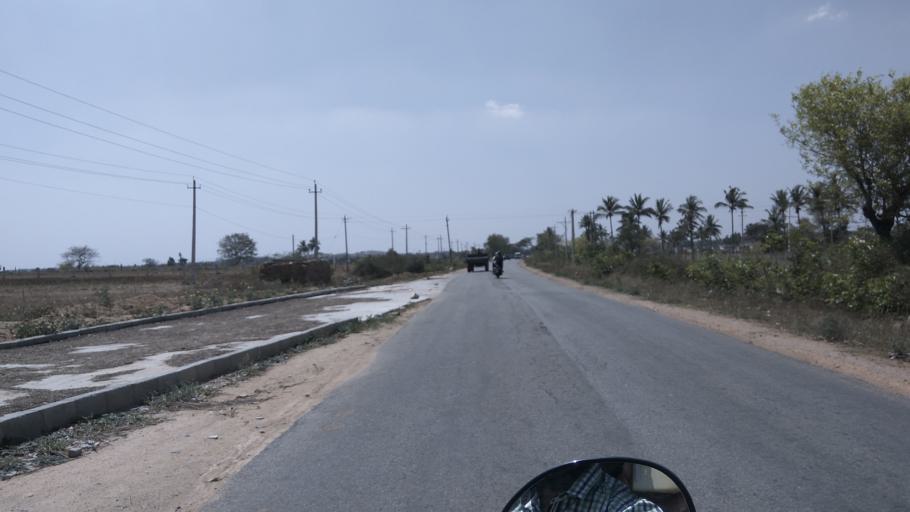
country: IN
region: Karnataka
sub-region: Kolar
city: Mulbagal
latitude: 13.1653
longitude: 78.3701
